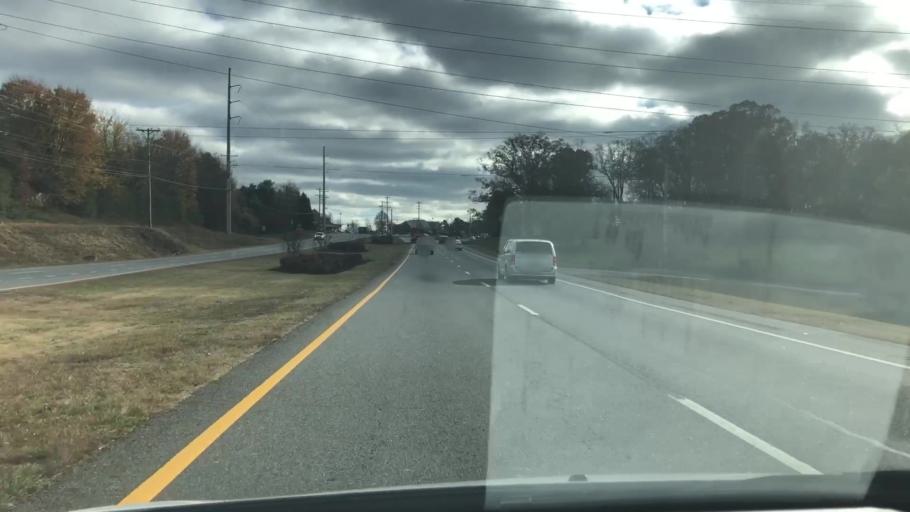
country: US
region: Georgia
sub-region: Forsyth County
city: Cumming
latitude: 34.1279
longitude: -84.1713
